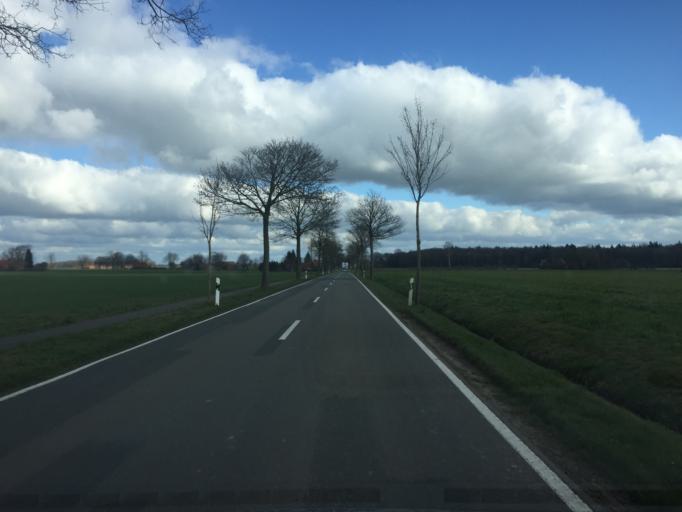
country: DE
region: Lower Saxony
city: Schwaforden
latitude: 52.7619
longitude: 8.8455
